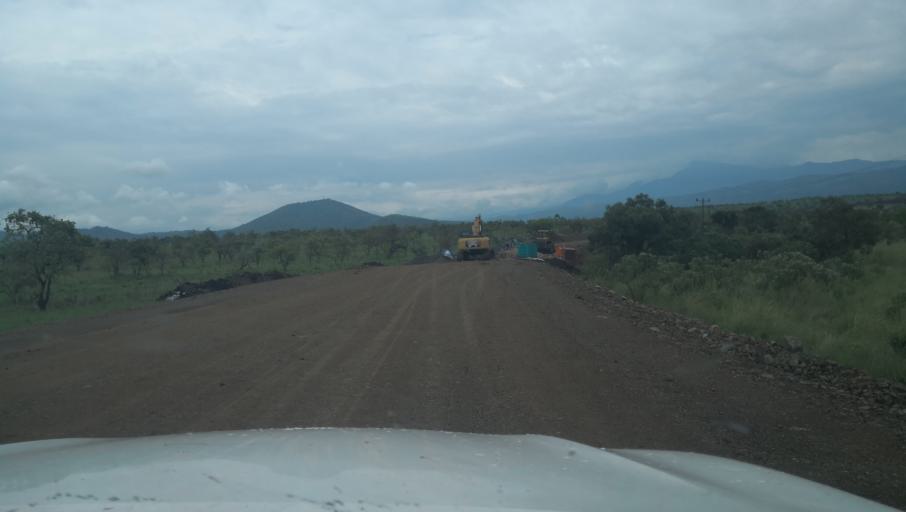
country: ET
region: Southern Nations, Nationalities, and People's Region
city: Felege Neway
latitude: 6.4234
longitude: 37.2401
